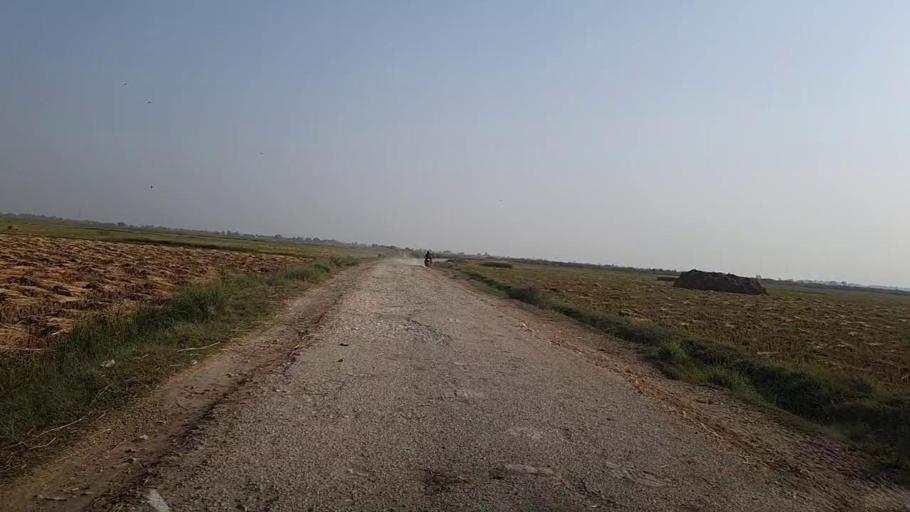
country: PK
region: Sindh
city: Kandhkot
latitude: 28.2988
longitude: 69.2519
